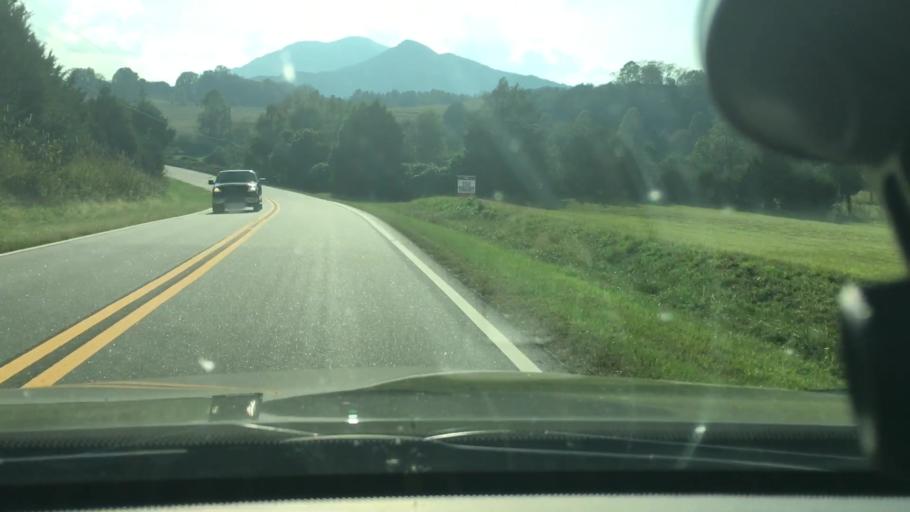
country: US
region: North Carolina
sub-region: Polk County
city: Columbus
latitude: 35.3108
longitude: -82.1474
